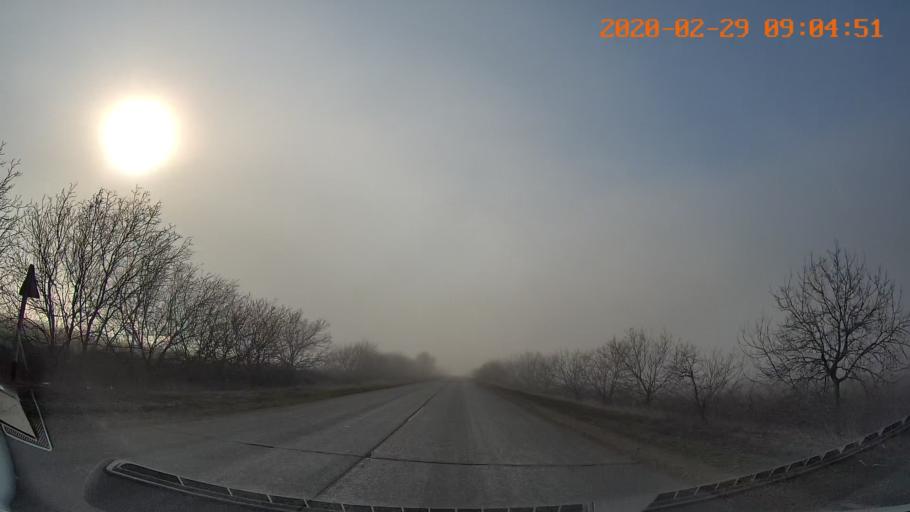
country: MD
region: Telenesti
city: Tiraspolul Nou
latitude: 46.8968
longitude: 29.7379
